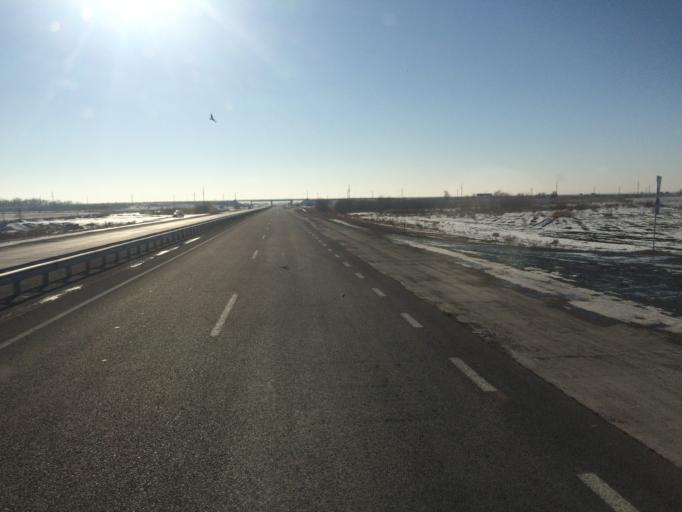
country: KG
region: Chuy
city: Sokuluk
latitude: 43.2810
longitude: 74.2353
